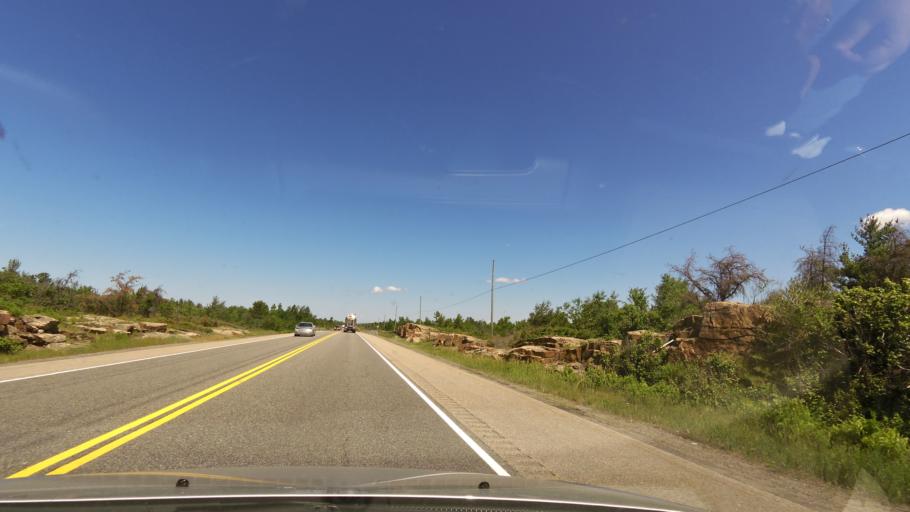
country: CA
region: Ontario
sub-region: Parry Sound District
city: Parry Sound
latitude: 45.7443
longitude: -80.4828
